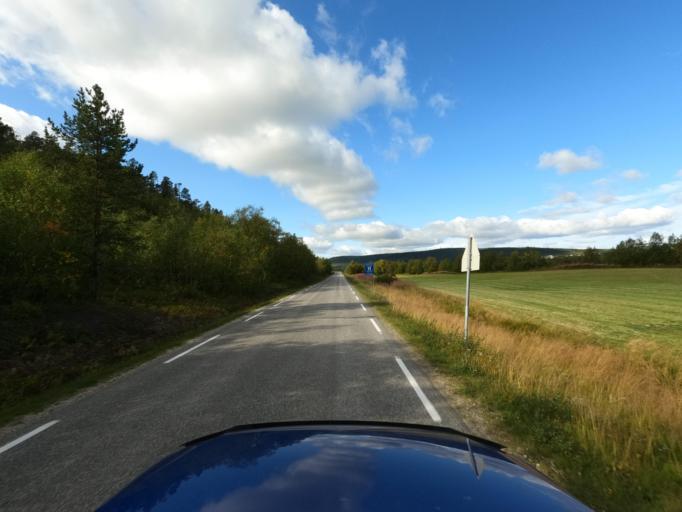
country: NO
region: Finnmark Fylke
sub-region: Karasjok
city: Karasjohka
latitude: 69.4589
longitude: 25.5441
